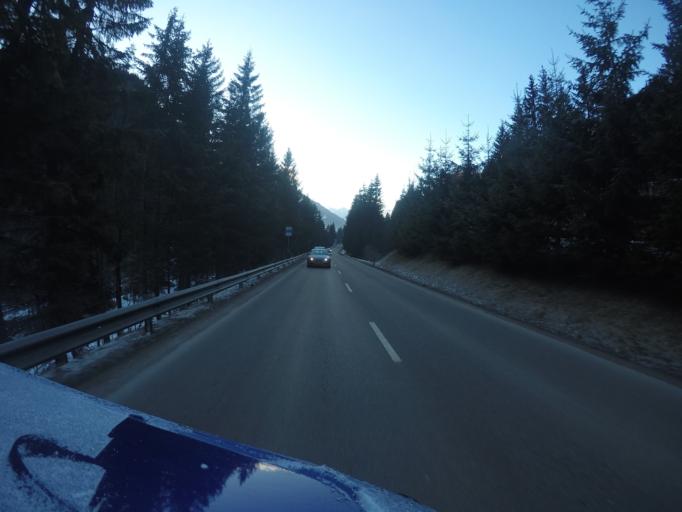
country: IT
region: Trentino-Alto Adige
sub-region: Provincia di Trento
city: Mazzin
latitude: 46.4540
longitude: 11.6992
